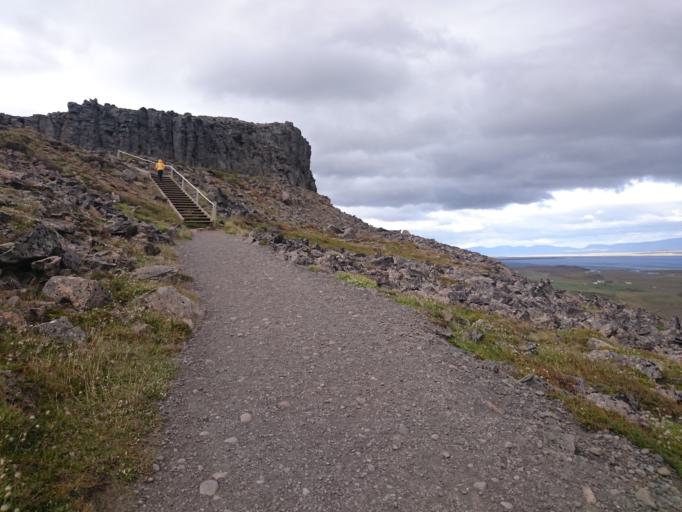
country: IS
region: Northwest
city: Saudarkrokur
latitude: 65.4744
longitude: -20.5963
